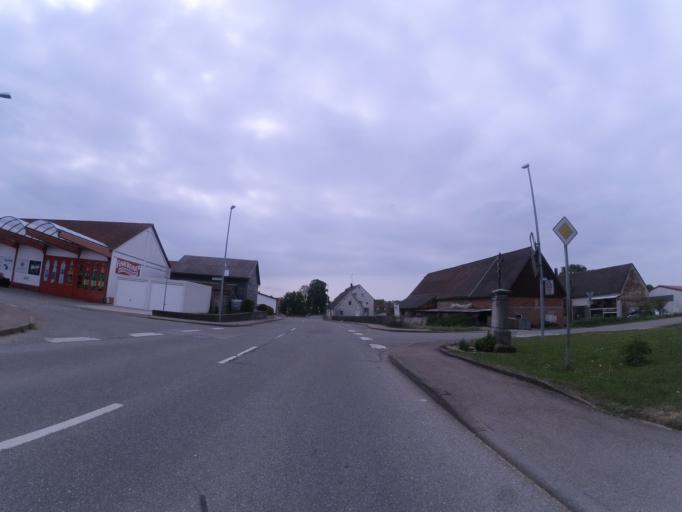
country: DE
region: Baden-Wuerttemberg
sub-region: Tuebingen Region
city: Staig
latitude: 48.3031
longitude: 9.9766
